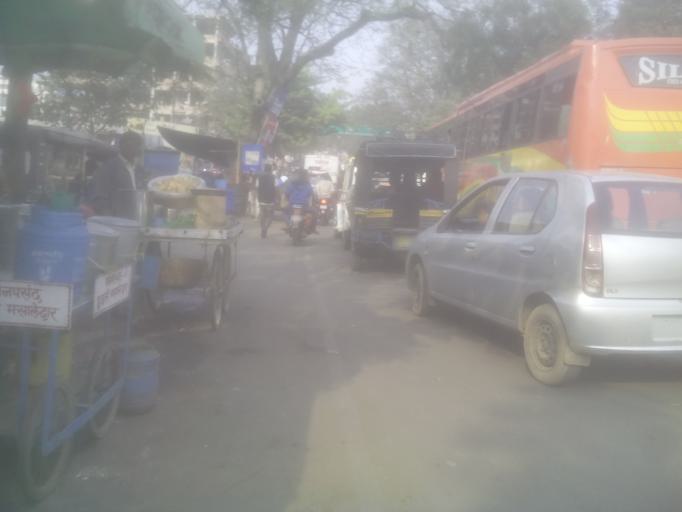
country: IN
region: Jharkhand
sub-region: Dhanbad
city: Dhanbad
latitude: 23.8058
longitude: 86.4311
